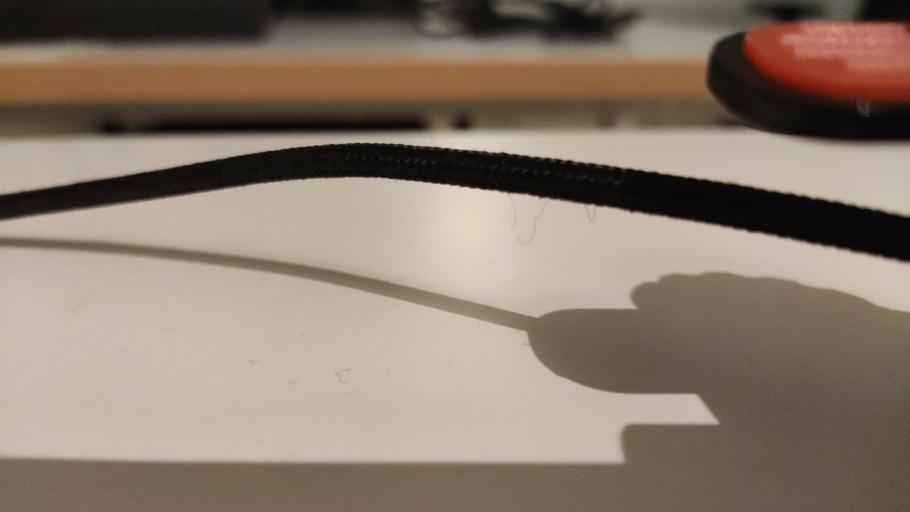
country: RU
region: Moskovskaya
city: Gorshkovo
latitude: 56.3717
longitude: 37.4231
